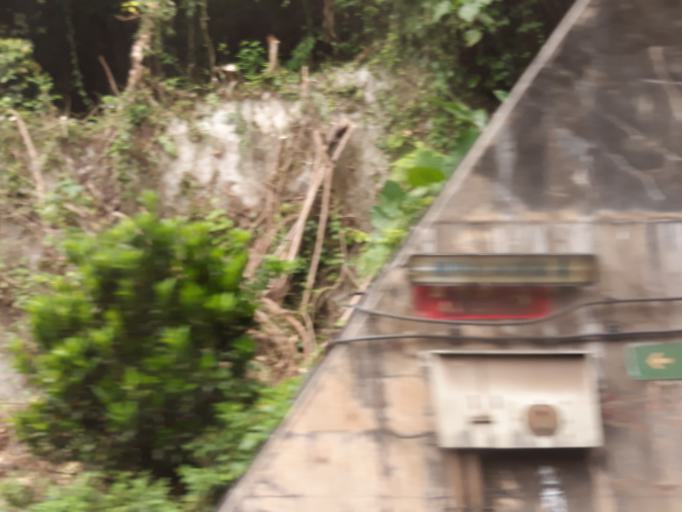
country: TW
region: Taiwan
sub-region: Yilan
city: Yilan
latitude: 24.4508
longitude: 121.7757
